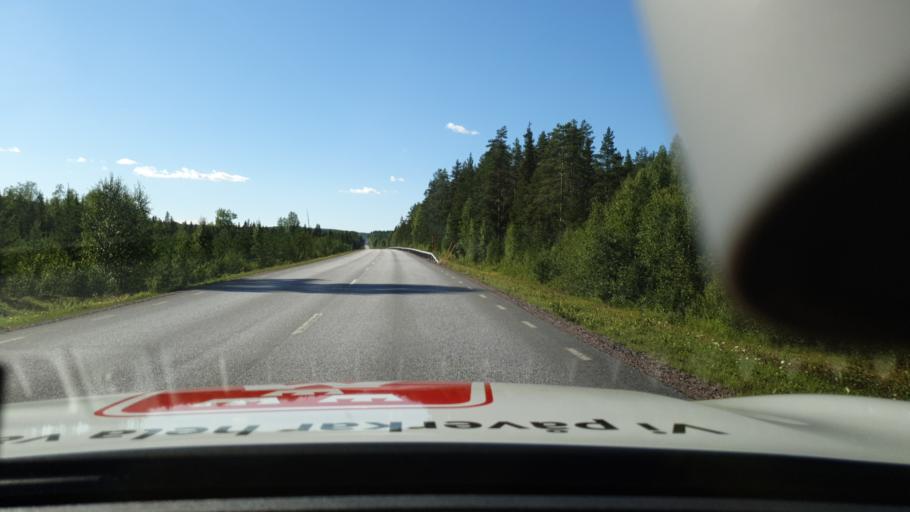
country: SE
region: Norrbotten
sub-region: Pitea Kommun
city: Norrfjarden
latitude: 65.6050
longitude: 21.4764
